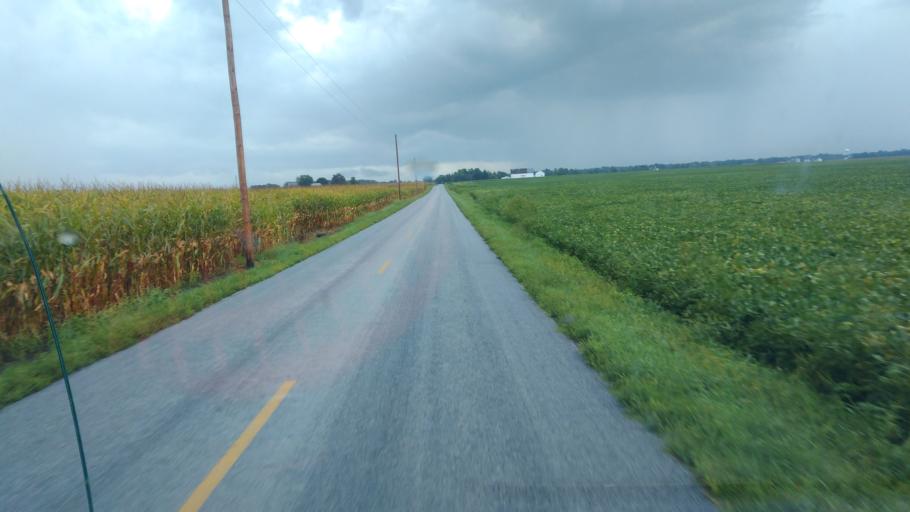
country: US
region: Ohio
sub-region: Hardin County
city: Kenton
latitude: 40.6839
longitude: -83.5951
